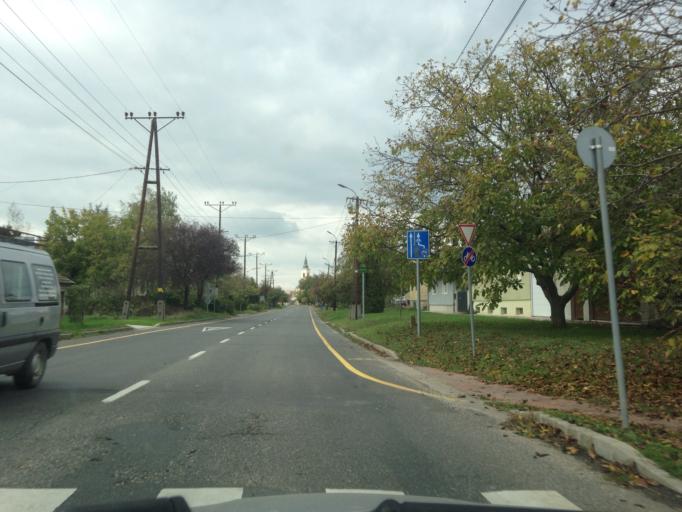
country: HU
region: Gyor-Moson-Sopron
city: Rajka
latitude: 47.9108
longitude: 17.1684
